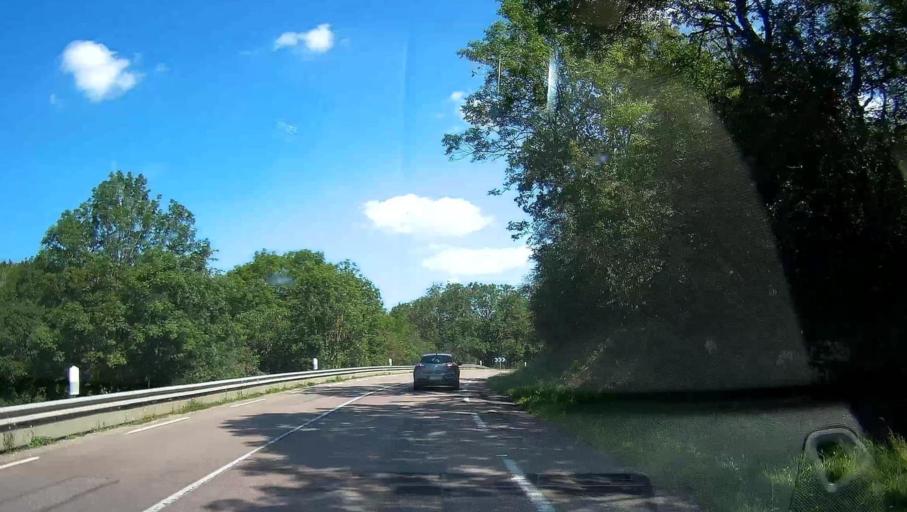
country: FR
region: Bourgogne
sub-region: Departement de la Cote-d'Or
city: Nolay
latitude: 46.9642
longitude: 4.6916
